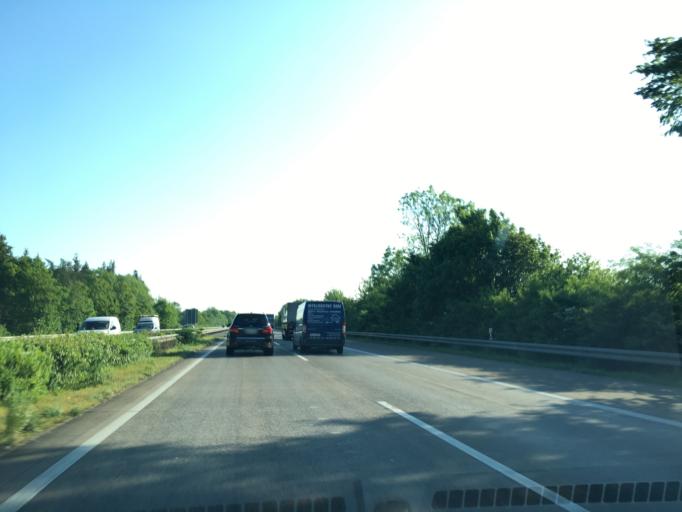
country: DE
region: North Rhine-Westphalia
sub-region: Regierungsbezirk Munster
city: Ladbergen
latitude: 52.1517
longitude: 7.7369
